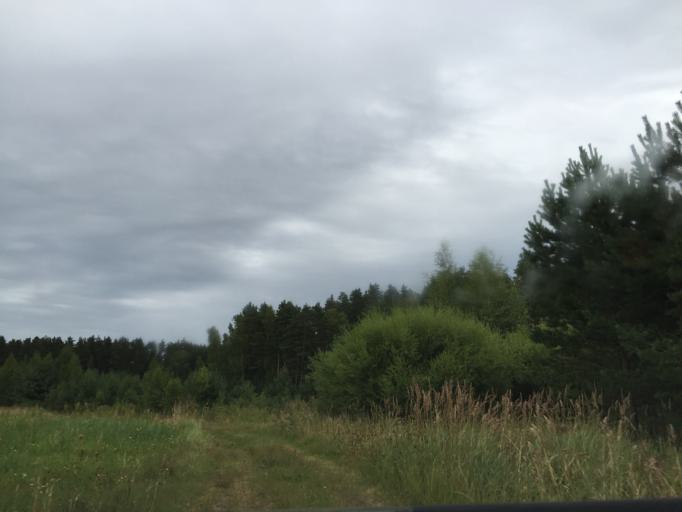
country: LV
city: Tireli
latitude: 56.8449
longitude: 23.6039
